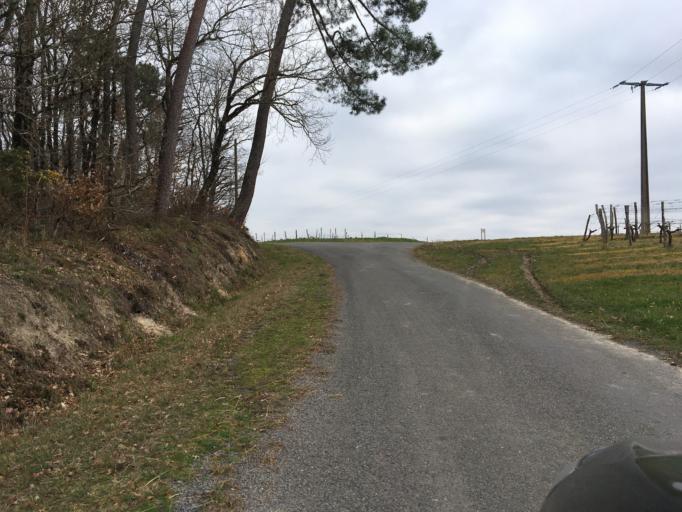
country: FR
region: Aquitaine
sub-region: Departement de la Gironde
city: Saint-Ciers-sur-Gironde
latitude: 45.3185
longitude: -0.6020
